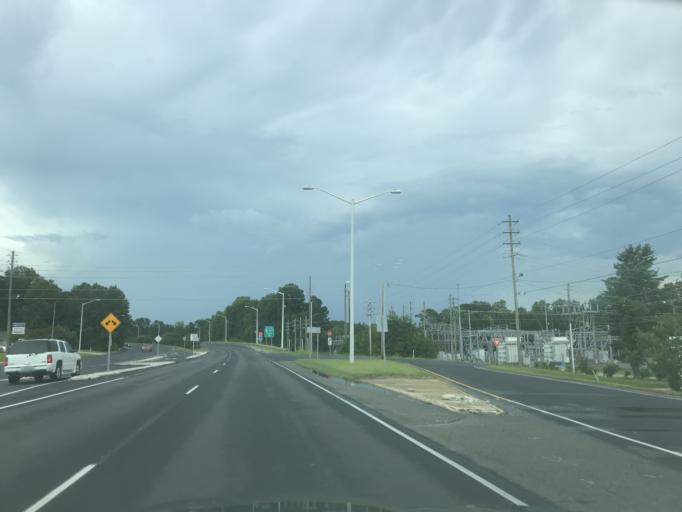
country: US
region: North Carolina
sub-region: Johnston County
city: Clayton
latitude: 35.6481
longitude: -78.4673
